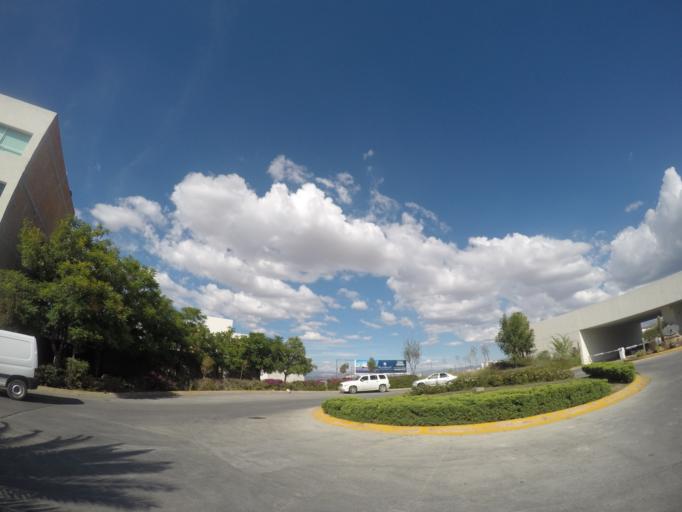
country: MX
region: San Luis Potosi
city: Escalerillas
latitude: 22.1215
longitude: -101.0324
